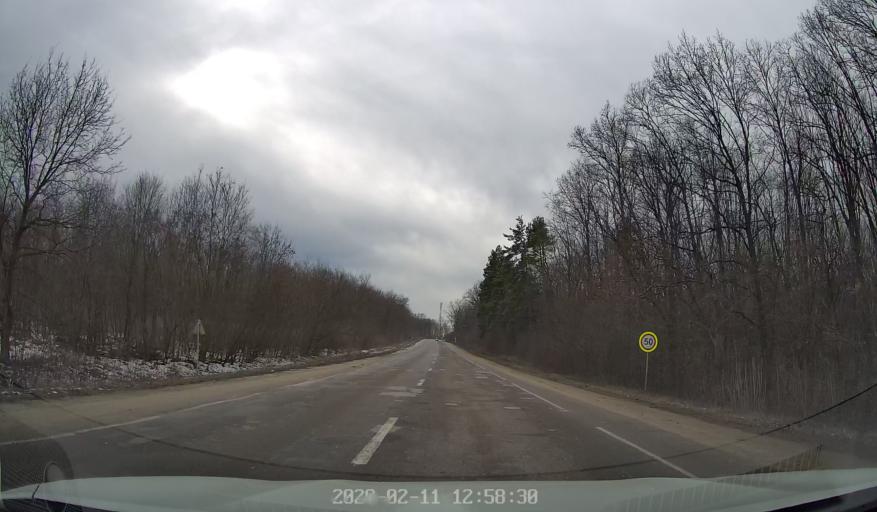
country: MD
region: Briceni
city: Briceni
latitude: 48.3344
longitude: 27.0517
